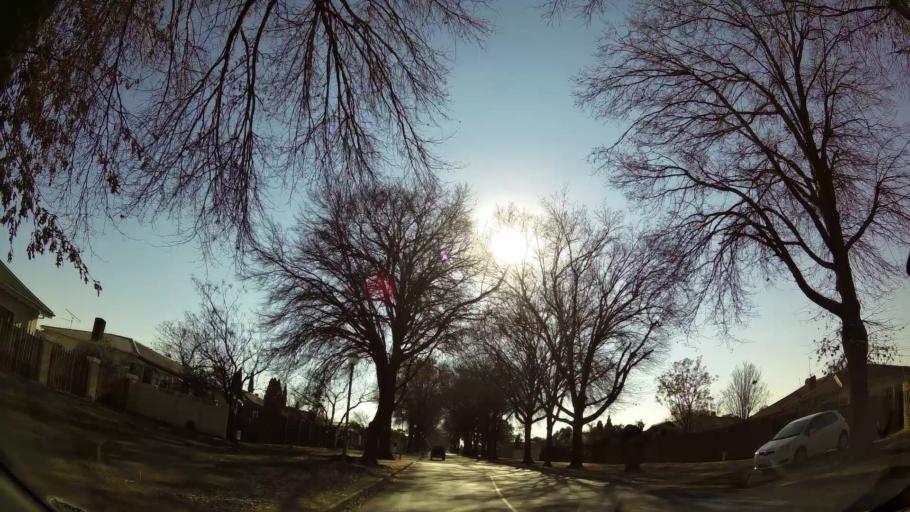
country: ZA
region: Gauteng
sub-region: Ekurhuleni Metropolitan Municipality
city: Benoni
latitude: -26.1642
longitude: 28.3128
